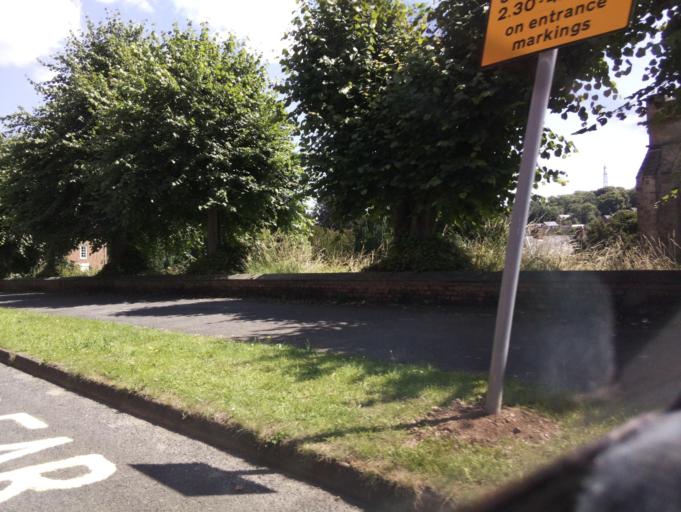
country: GB
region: England
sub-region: Derbyshire
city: Ashbourne
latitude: 53.0154
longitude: -1.7386
